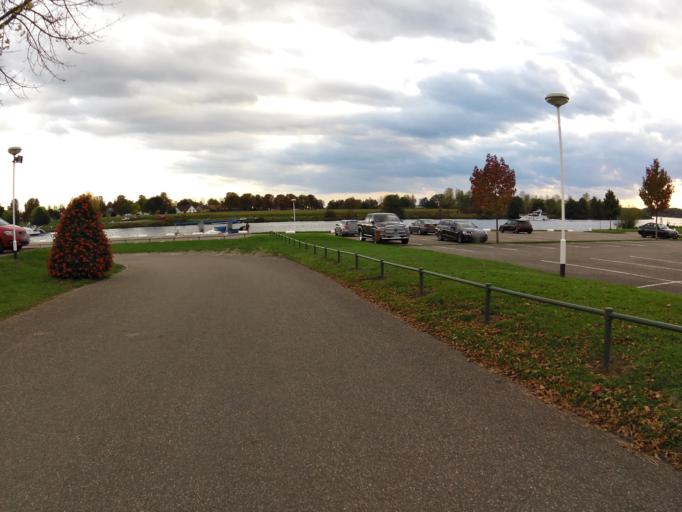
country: NL
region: Limburg
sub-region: Gemeente Roermond
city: Roermond
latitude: 51.1917
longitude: 5.9497
